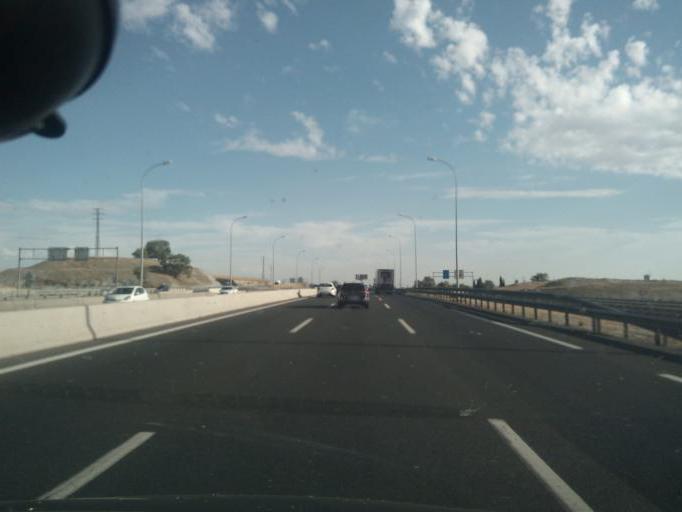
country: ES
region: Madrid
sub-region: Provincia de Madrid
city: Pinto
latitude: 40.2332
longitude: -3.6896
